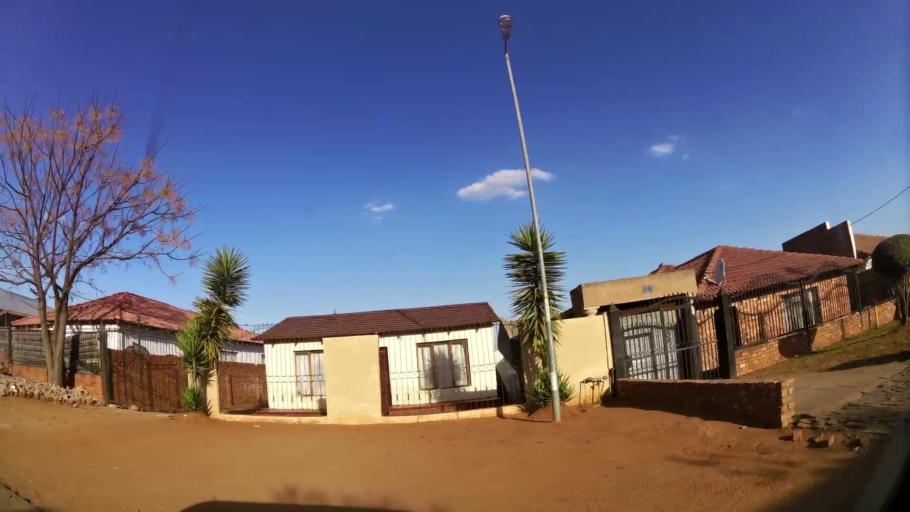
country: ZA
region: Gauteng
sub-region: City of Tshwane Metropolitan Municipality
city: Cullinan
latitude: -25.7041
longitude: 28.3868
